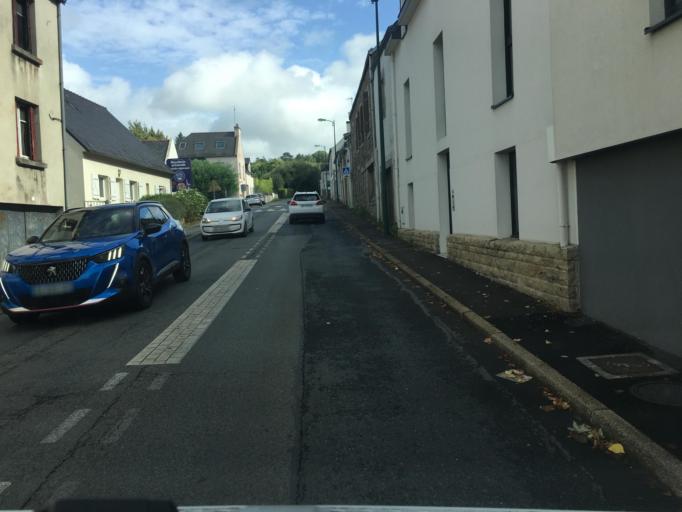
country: FR
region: Brittany
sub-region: Departement du Finistere
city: La Foret-Fouesnant
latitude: 47.9103
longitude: -3.9771
